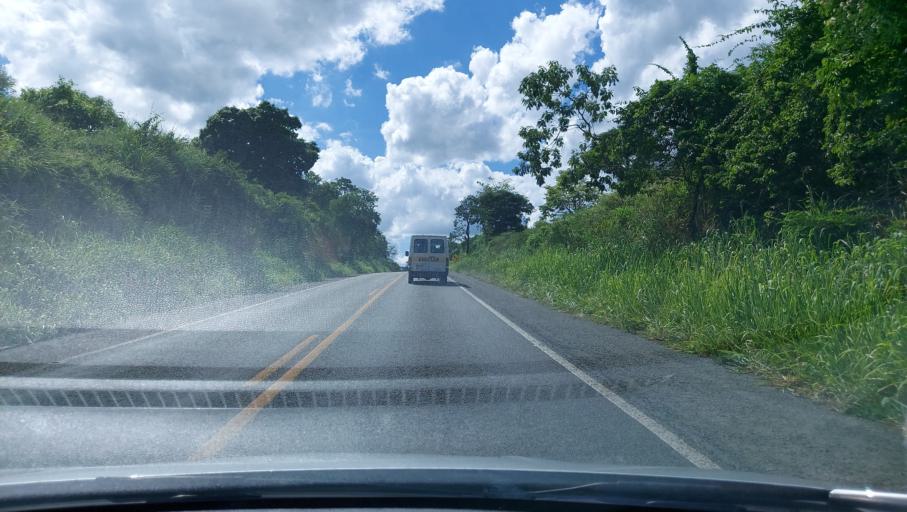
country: BR
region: Bahia
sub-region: Ruy Barbosa
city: Terra Nova
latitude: -12.4443
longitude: -40.8694
